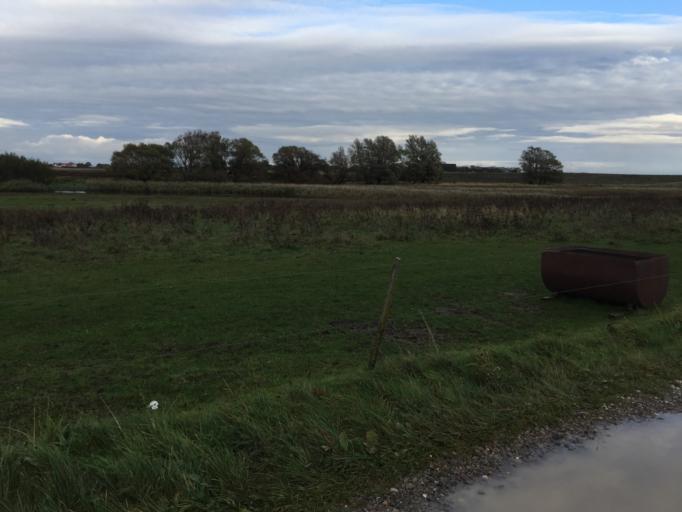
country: DK
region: Zealand
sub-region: Slagelse Kommune
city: Skaelskor
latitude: 55.2071
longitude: 11.1779
